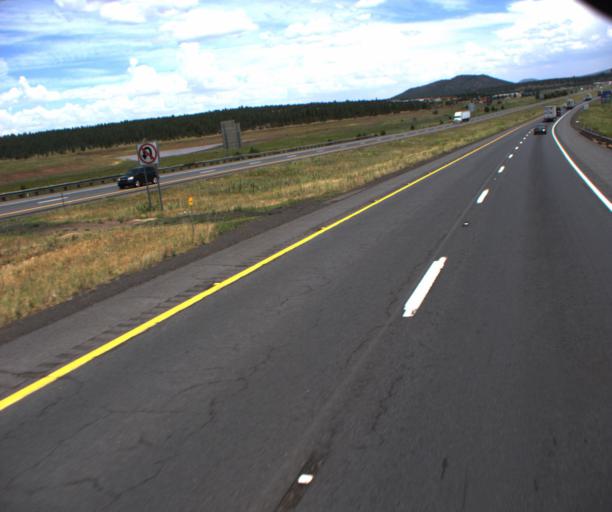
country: US
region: Arizona
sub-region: Coconino County
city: Williams
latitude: 35.2522
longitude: -112.2057
